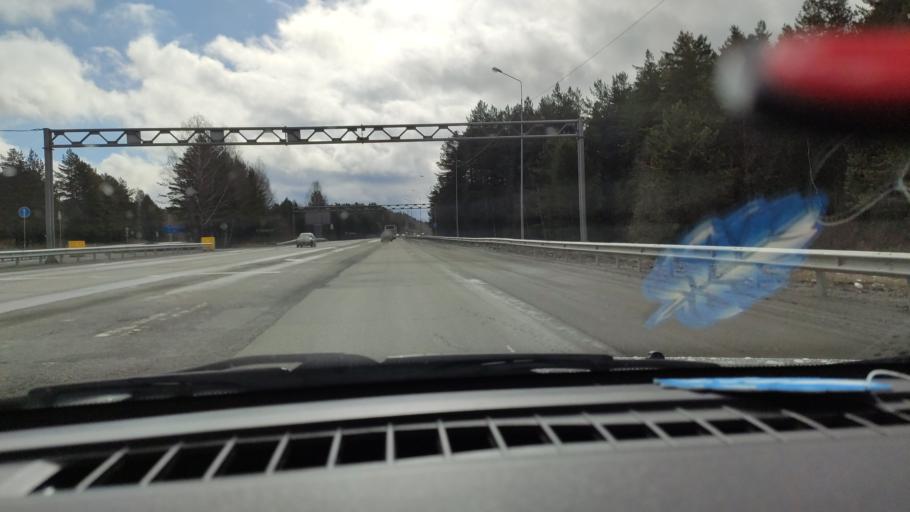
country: RU
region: Sverdlovsk
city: Talitsa
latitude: 56.8724
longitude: 60.0364
